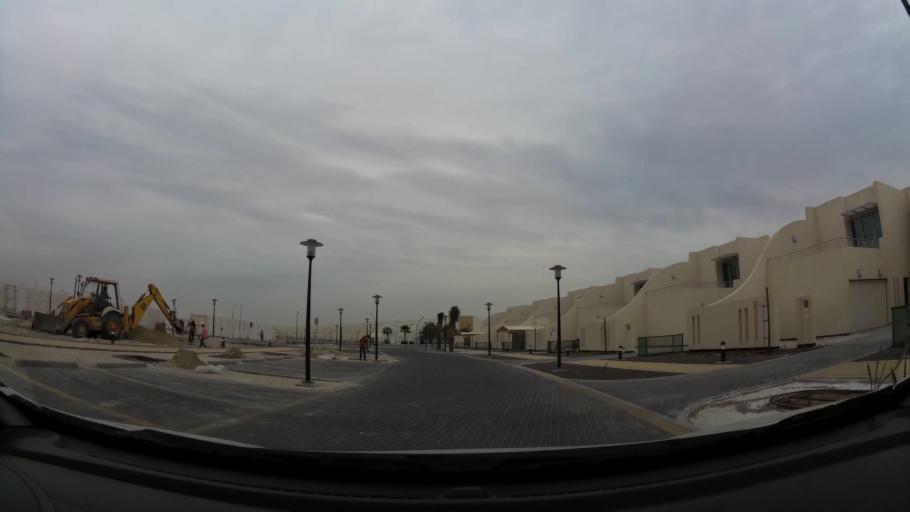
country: BH
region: Central Governorate
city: Dar Kulayb
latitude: 25.8292
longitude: 50.6114
